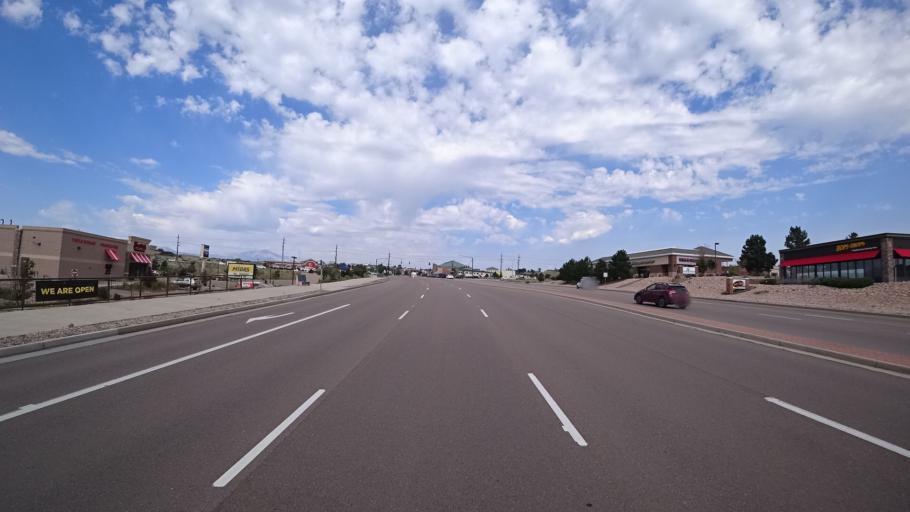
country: US
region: Colorado
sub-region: El Paso County
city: Cimarron Hills
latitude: 38.9107
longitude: -104.7174
